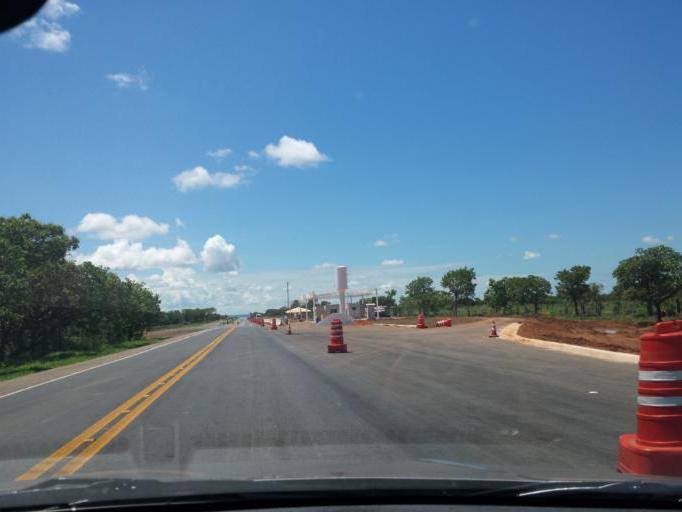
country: BR
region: Goias
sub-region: Luziania
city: Luziania
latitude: -16.4538
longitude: -47.8077
